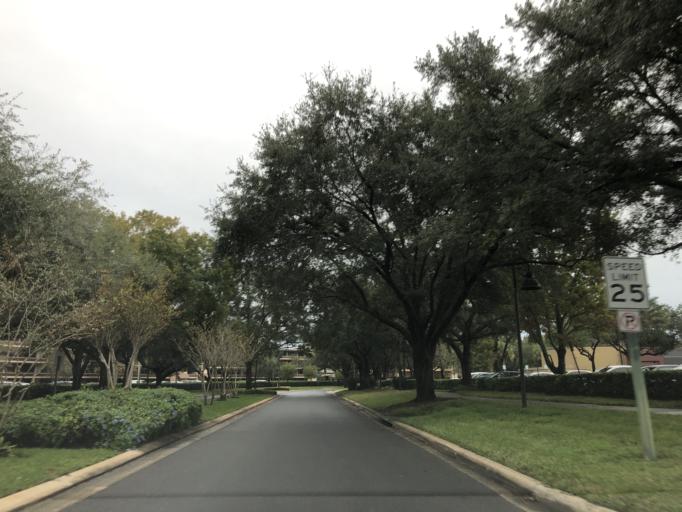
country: US
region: Florida
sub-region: Orange County
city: Doctor Phillips
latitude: 28.4318
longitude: -81.4723
